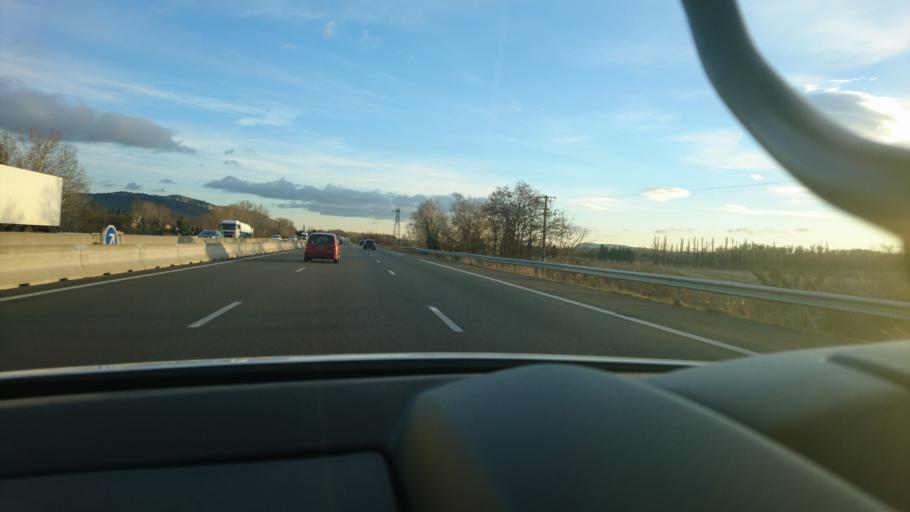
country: FR
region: Provence-Alpes-Cote d'Azur
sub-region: Departement du Vaucluse
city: Mondragon
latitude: 44.2295
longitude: 4.7096
